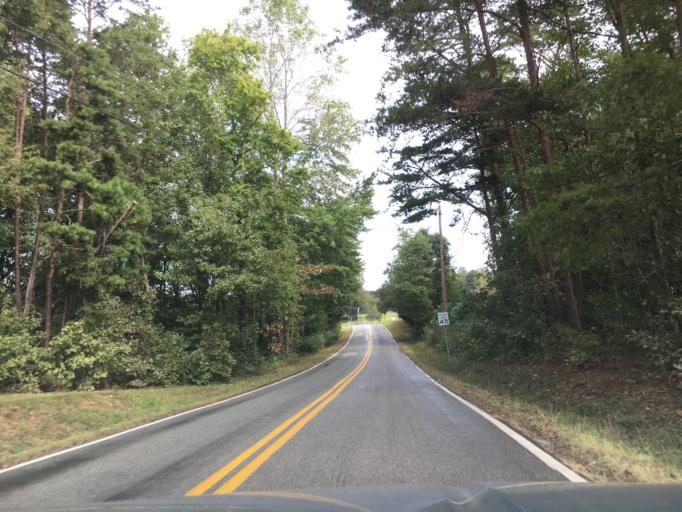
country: US
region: Virginia
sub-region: Goochland County
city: Goochland
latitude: 37.7104
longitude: -77.8418
